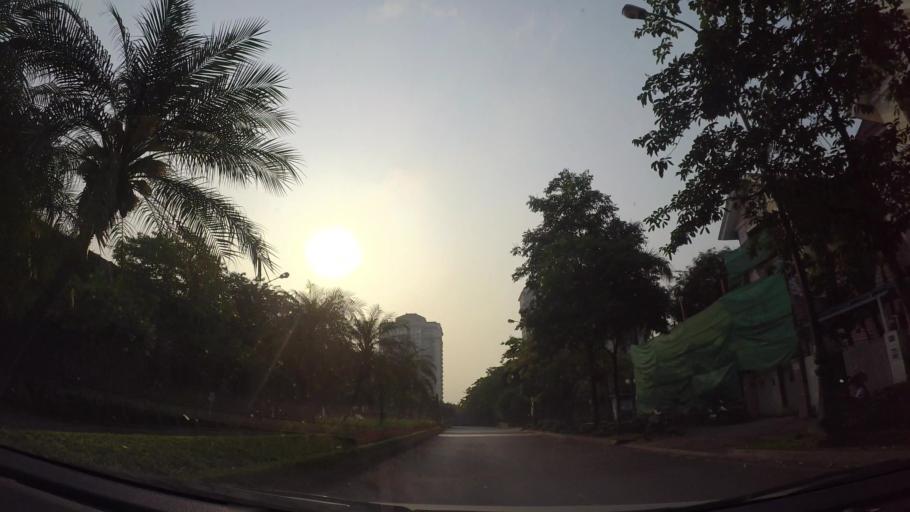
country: VN
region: Ha Noi
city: Tay Ho
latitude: 21.0772
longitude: 105.7953
